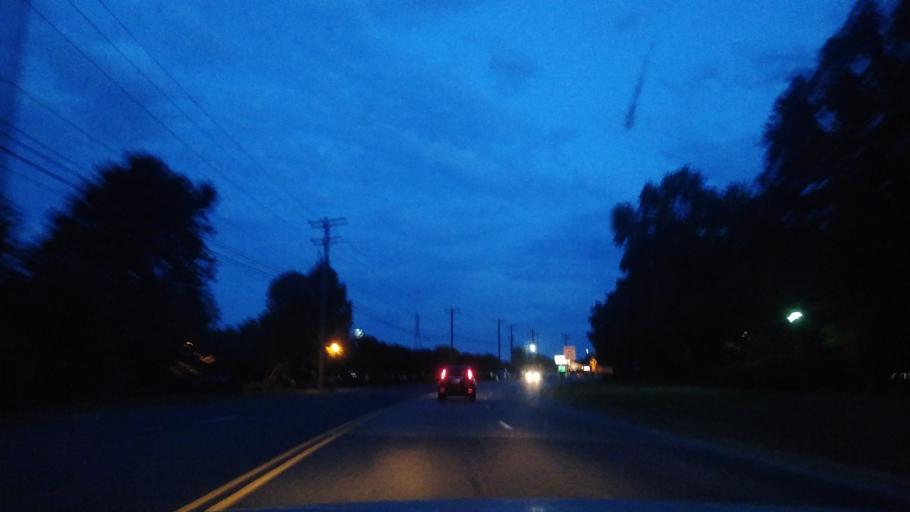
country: US
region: North Carolina
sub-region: Guilford County
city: Jamestown
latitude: 36.0662
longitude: -79.9098
